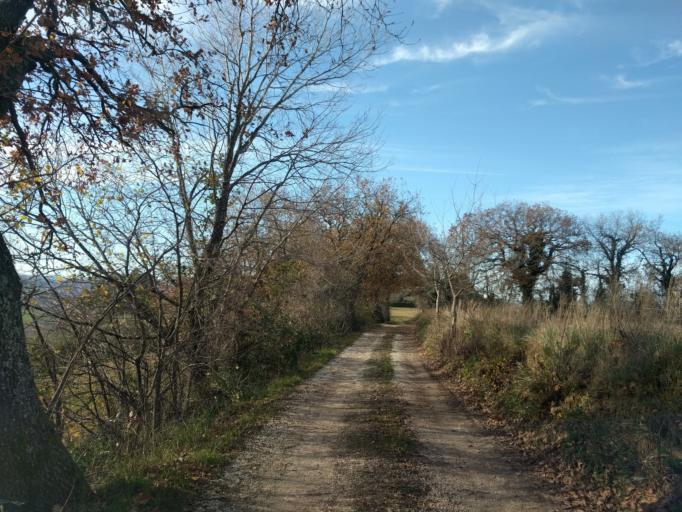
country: IT
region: The Marches
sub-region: Provincia di Pesaro e Urbino
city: Cuccurano
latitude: 43.8097
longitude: 12.9605
